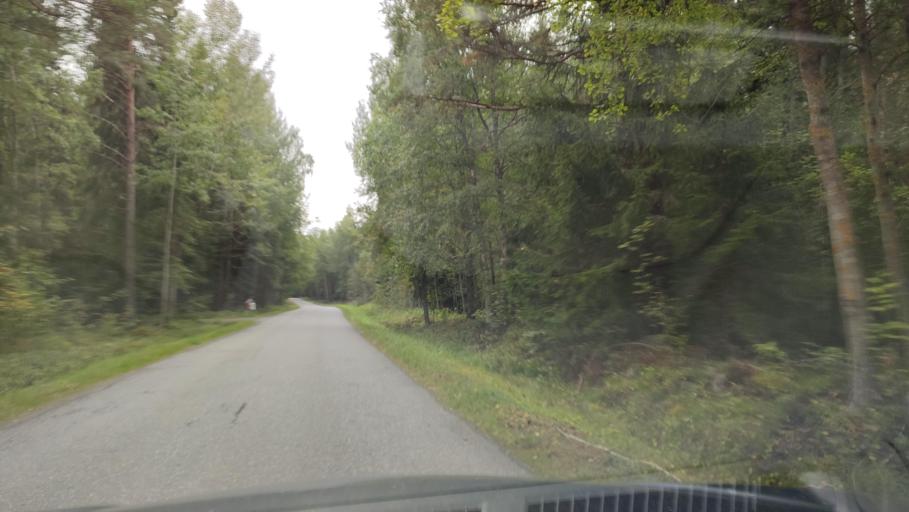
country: FI
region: Ostrobothnia
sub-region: Sydosterbotten
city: Kristinestad
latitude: 62.2515
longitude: 21.3523
